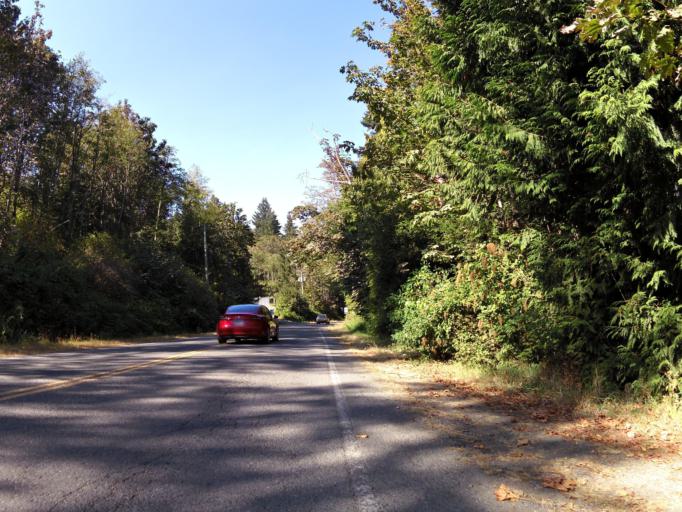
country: CA
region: British Columbia
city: North Saanich
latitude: 48.6172
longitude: -123.5220
